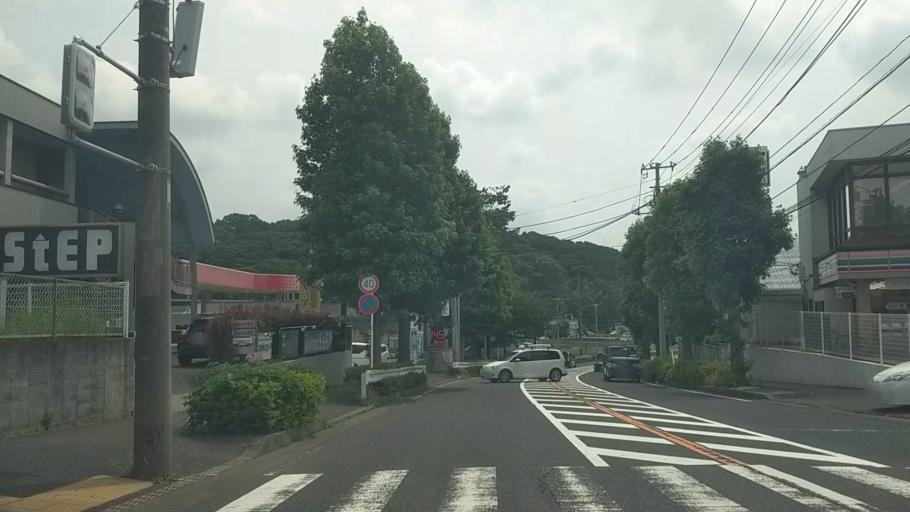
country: JP
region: Kanagawa
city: Fujisawa
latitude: 35.3601
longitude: 139.4479
